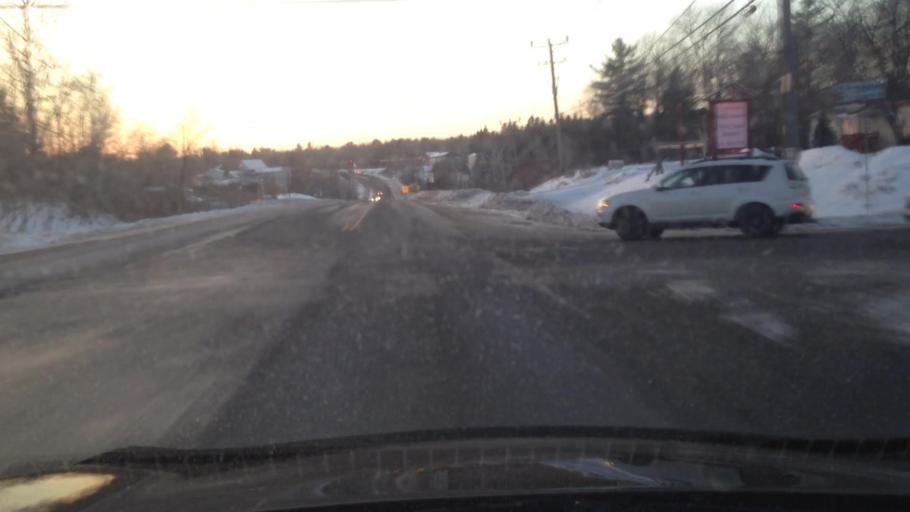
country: CA
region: Quebec
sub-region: Laurentides
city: Sainte-Sophie
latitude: 45.8325
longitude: -73.8739
